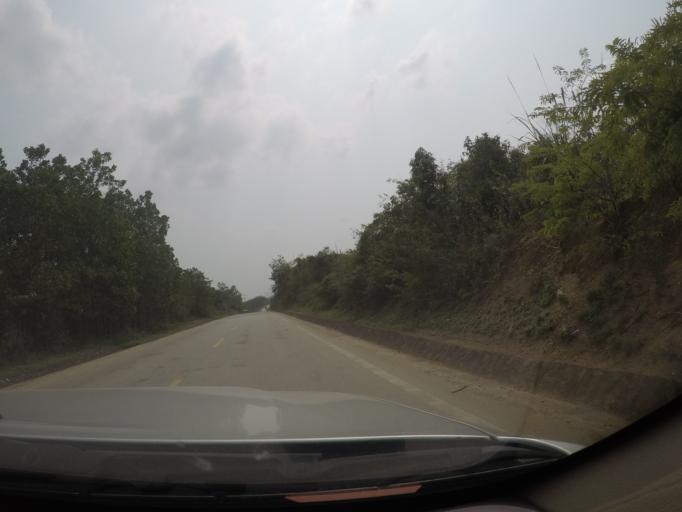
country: VN
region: Thanh Hoa
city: Thi Tran Yen Cat
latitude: 19.5191
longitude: 105.3985
